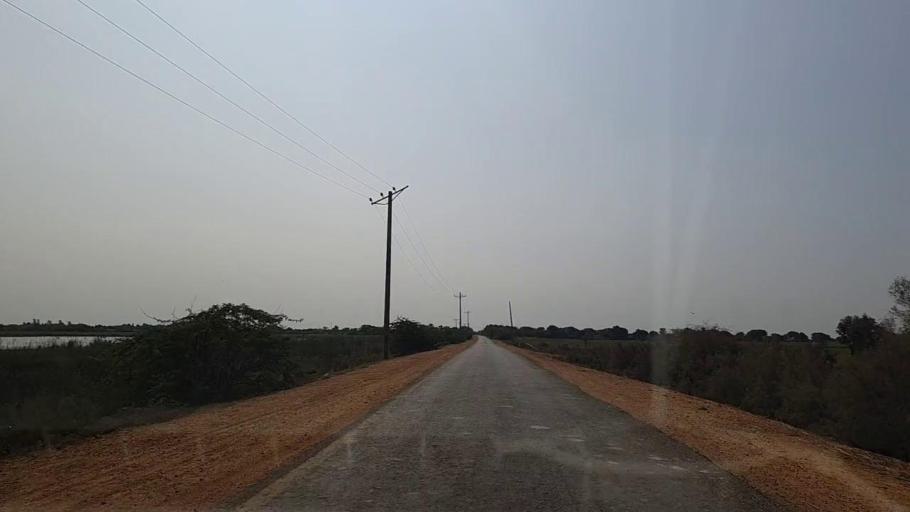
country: PK
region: Sindh
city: Chuhar Jamali
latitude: 24.3283
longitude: 67.9436
